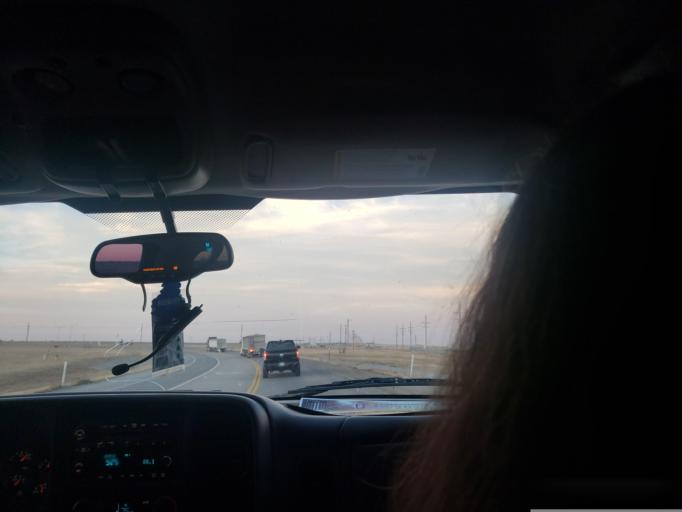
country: US
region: Kansas
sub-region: Seward County
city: Liberal
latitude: 37.0656
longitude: -100.9045
